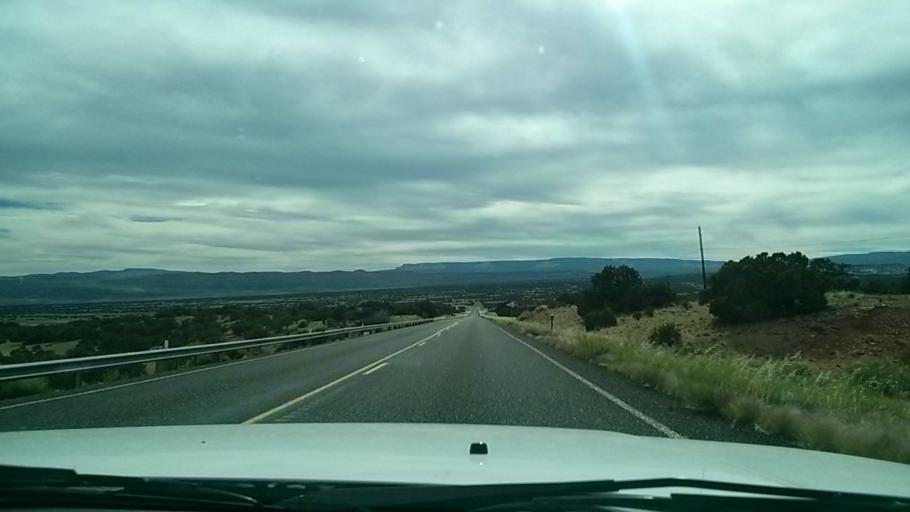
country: US
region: Utah
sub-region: Wayne County
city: Loa
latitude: 37.7504
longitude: -111.4706
